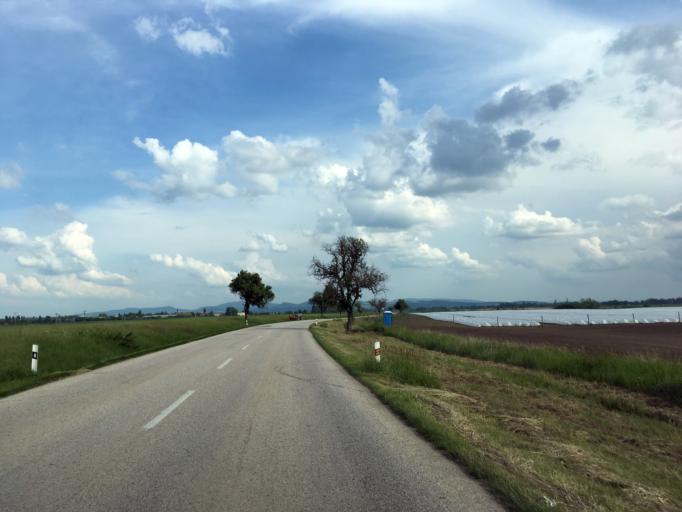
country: HU
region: Komarom-Esztergom
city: Almasfuzito
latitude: 47.7957
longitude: 18.2505
